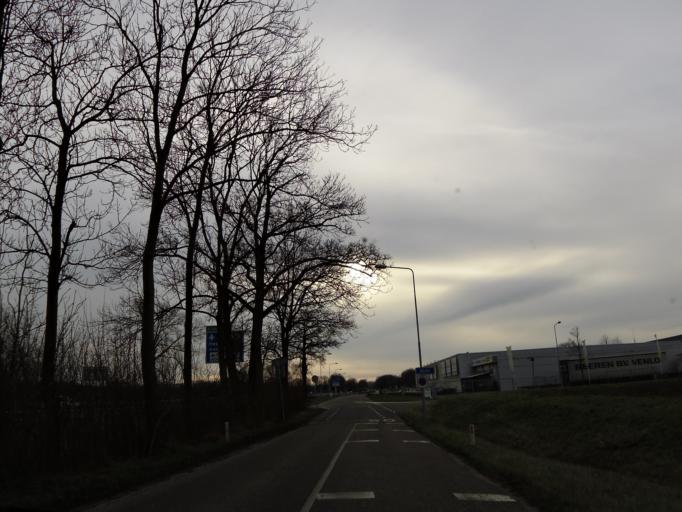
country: NL
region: Limburg
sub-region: Gemeente Nuth
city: Nuth
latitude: 50.9297
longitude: 5.8840
